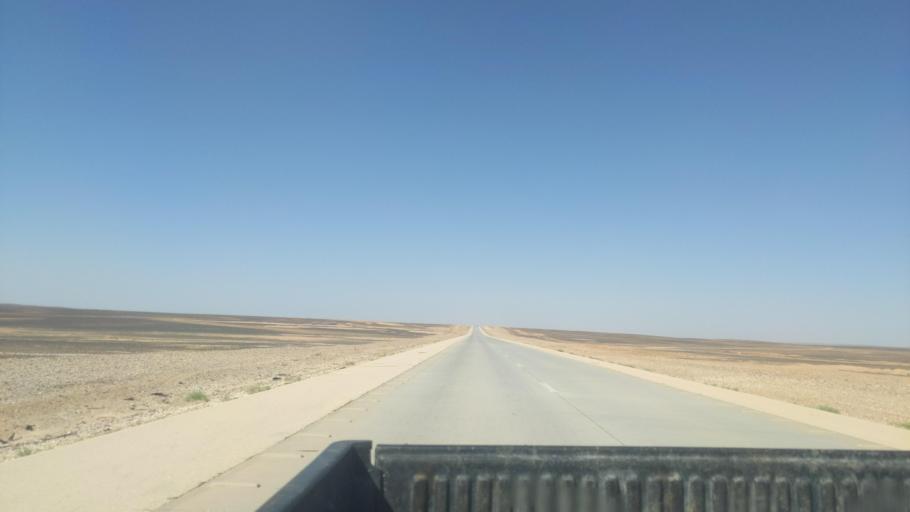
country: JO
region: Amman
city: Al Azraq ash Shamali
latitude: 31.4400
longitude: 36.7525
